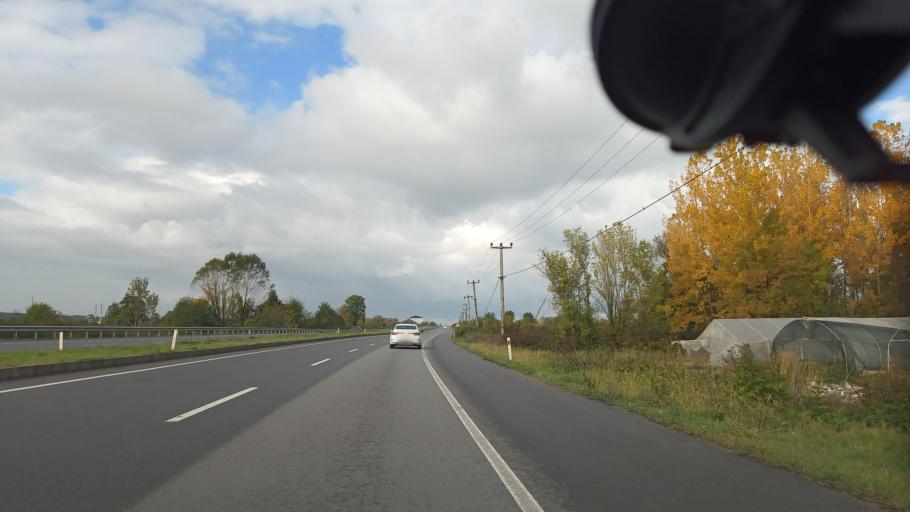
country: TR
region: Sakarya
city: Karasu
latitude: 41.0703
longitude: 30.7963
